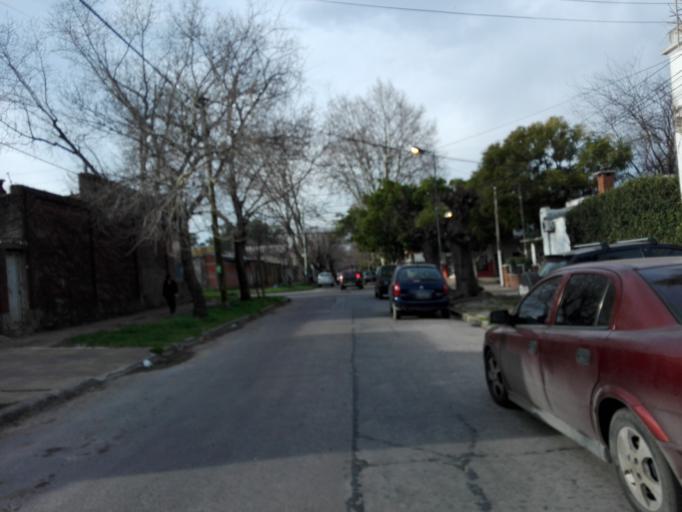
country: AR
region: Buenos Aires
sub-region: Partido de La Plata
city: La Plata
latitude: -34.8950
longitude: -57.9546
